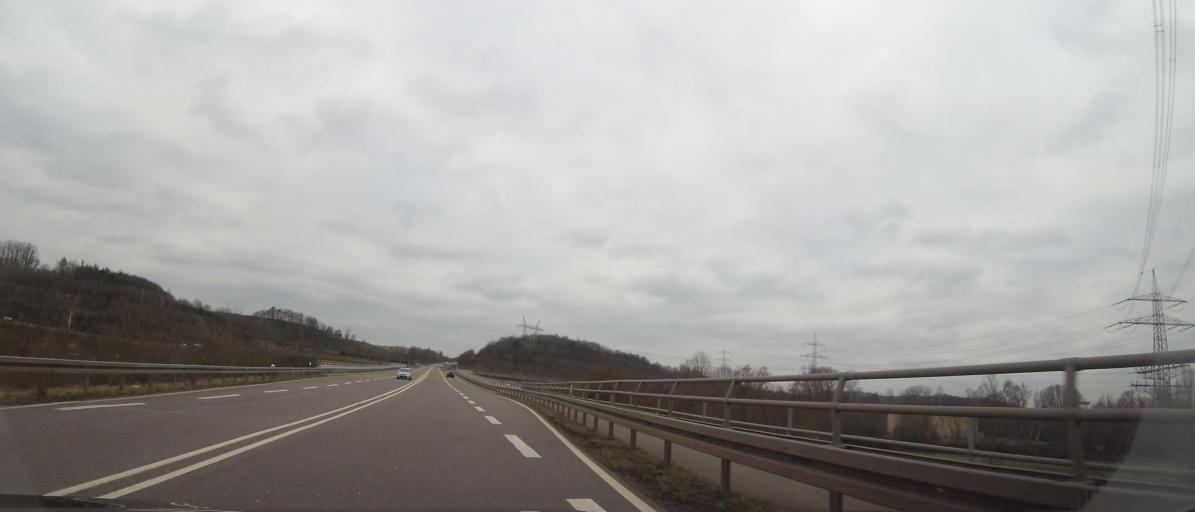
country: DE
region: Saarland
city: Ensdorf
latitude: 49.2851
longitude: 6.7695
